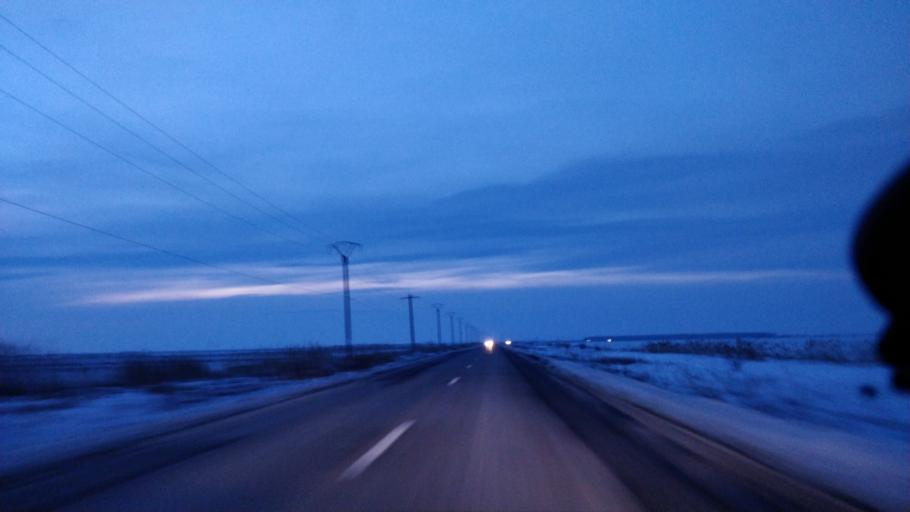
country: RO
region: Galati
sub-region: Comuna Liesti
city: Liesti
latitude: 45.5930
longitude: 27.4766
